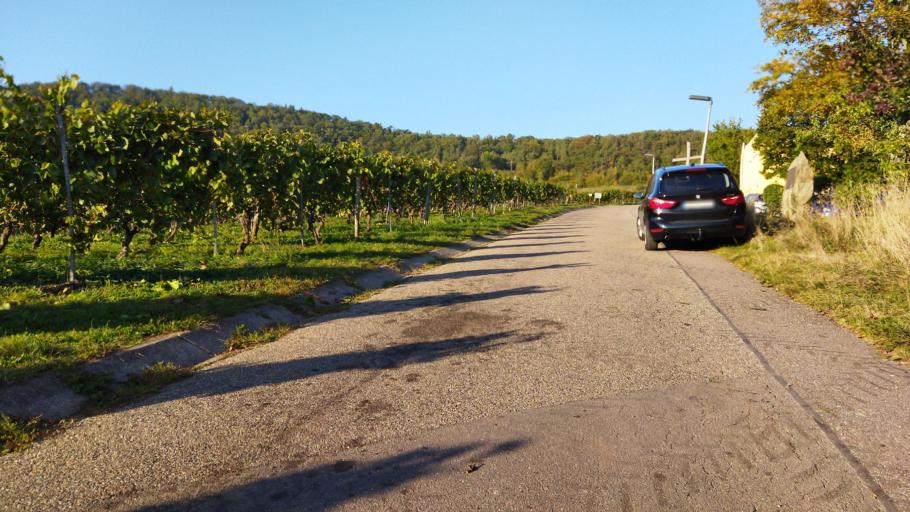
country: DE
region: Baden-Wuerttemberg
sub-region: Regierungsbezirk Stuttgart
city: Freudental
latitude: 49.0033
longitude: 9.0309
